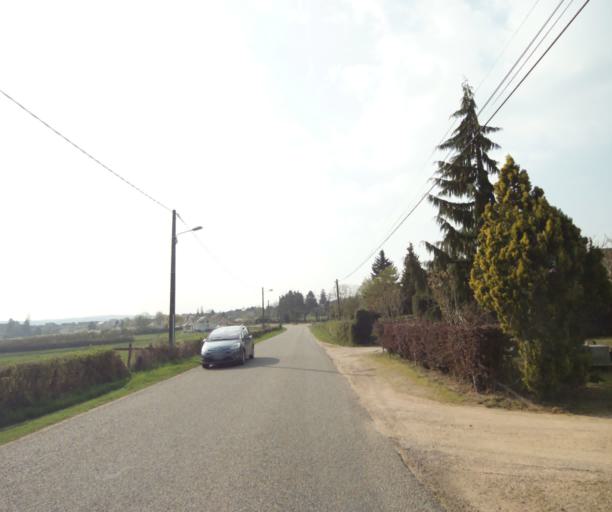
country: FR
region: Bourgogne
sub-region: Departement de Saone-et-Loire
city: Charolles
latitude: 46.4832
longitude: 4.4462
